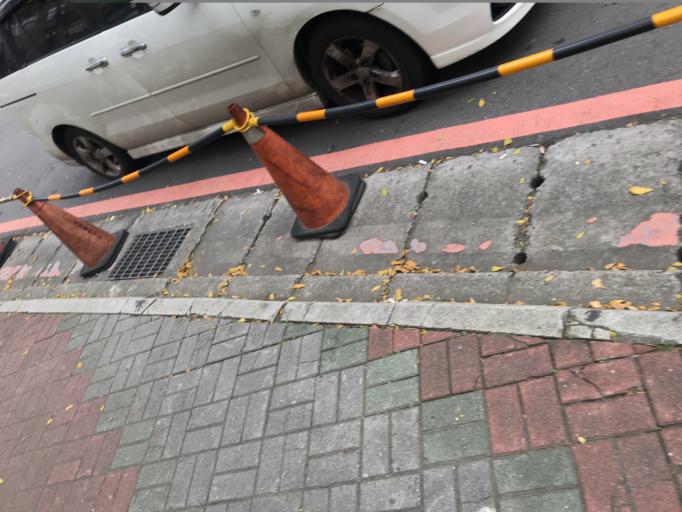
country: TW
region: Taipei
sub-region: Taipei
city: Banqiao
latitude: 25.0088
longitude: 121.4749
